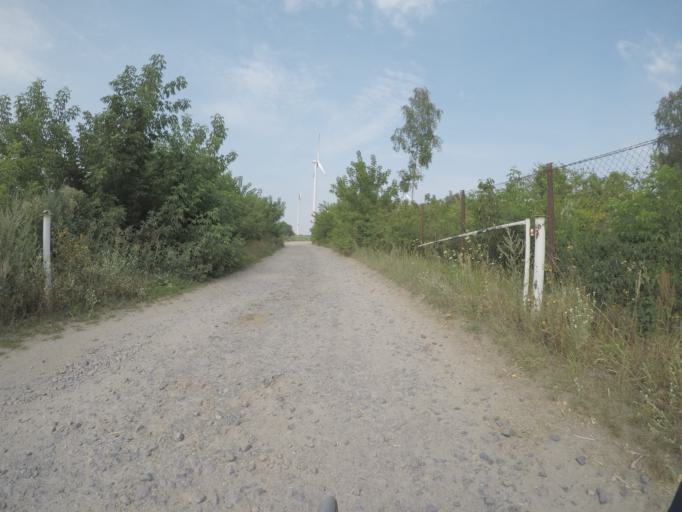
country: DE
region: Berlin
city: Blankenfelde
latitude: 52.6648
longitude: 13.4260
